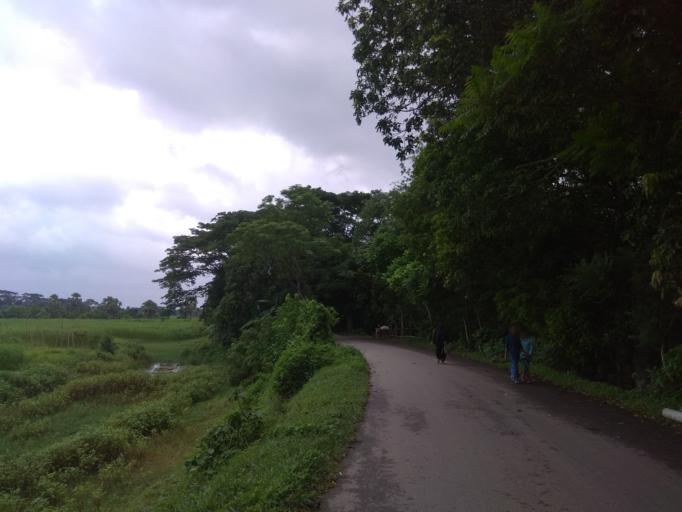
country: BD
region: Dhaka
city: Dohar
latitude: 23.4232
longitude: 90.0636
